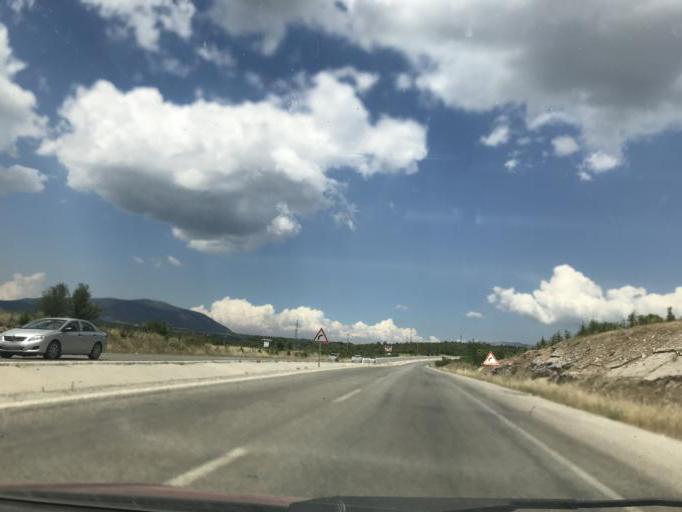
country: TR
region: Denizli
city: Tavas
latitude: 37.5894
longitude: 29.1064
